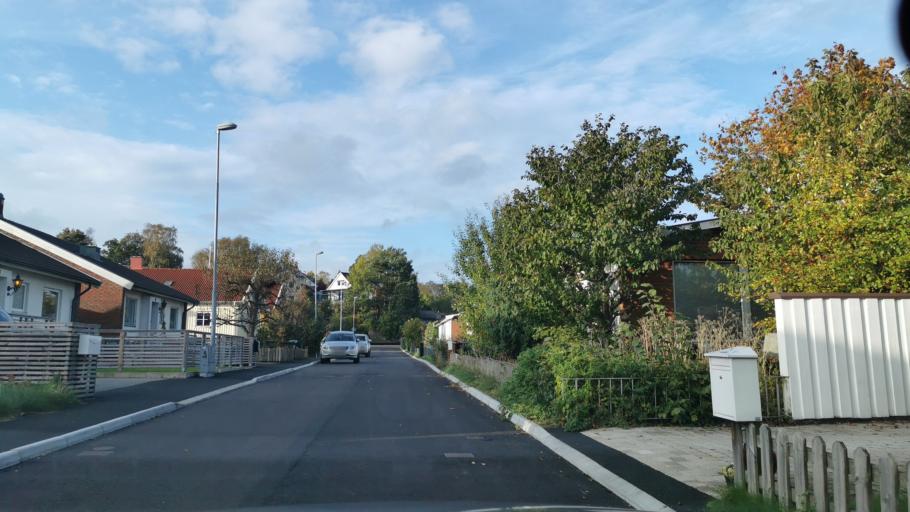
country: SE
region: Vaestra Goetaland
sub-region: Partille Kommun
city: Partille
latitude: 57.7236
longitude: 12.0759
